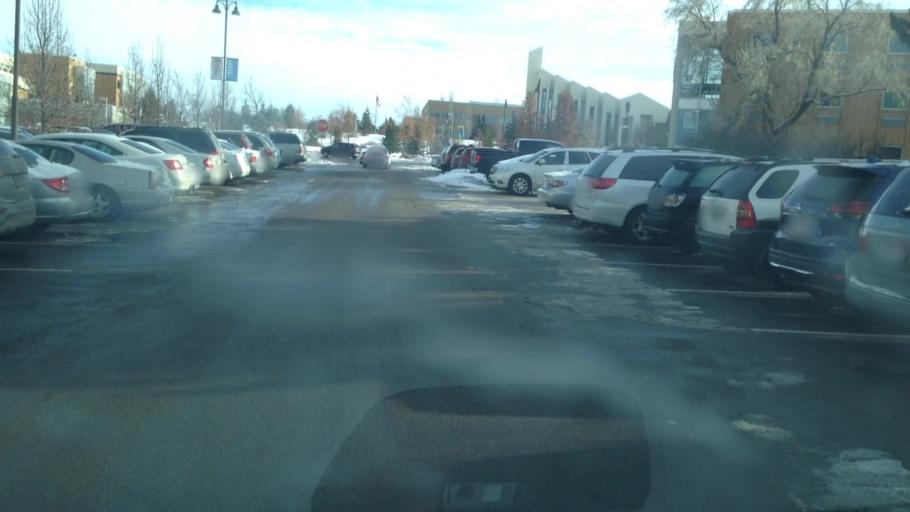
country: US
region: Idaho
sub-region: Madison County
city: Rexburg
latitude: 43.8176
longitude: -111.7850
